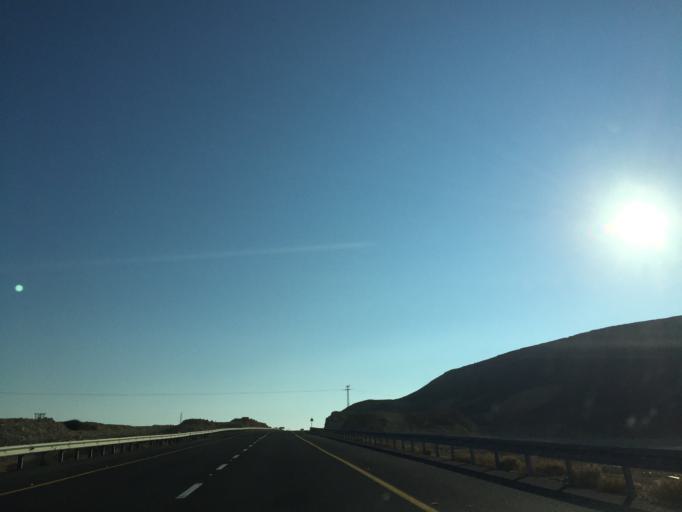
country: IL
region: Southern District
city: Mitzpe Ramon
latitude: 30.2992
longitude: 34.9699
